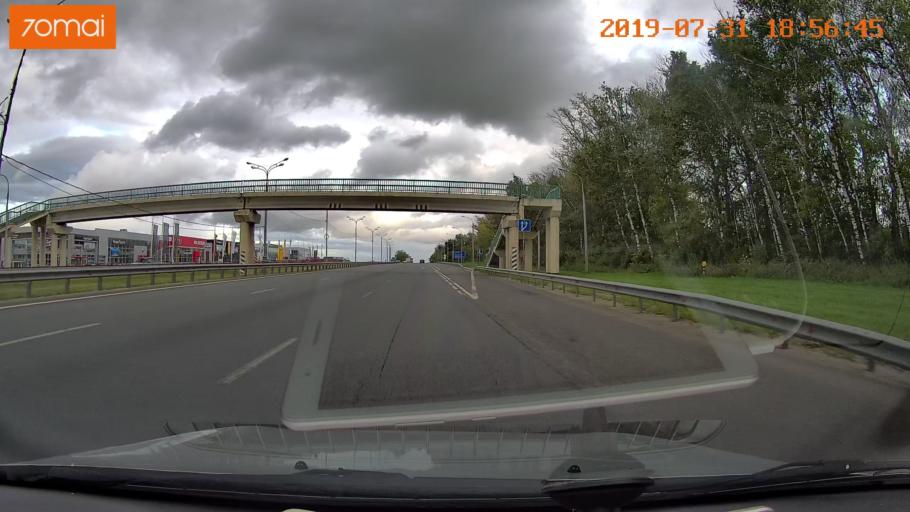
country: RU
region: Moskovskaya
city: Raduzhnyy
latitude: 55.1600
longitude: 38.6825
